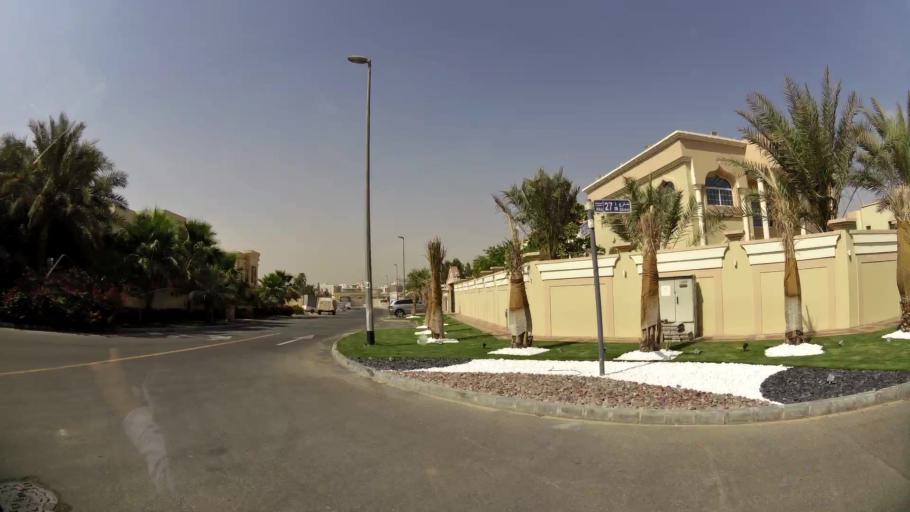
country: AE
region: Ash Shariqah
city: Sharjah
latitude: 25.2037
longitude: 55.4043
